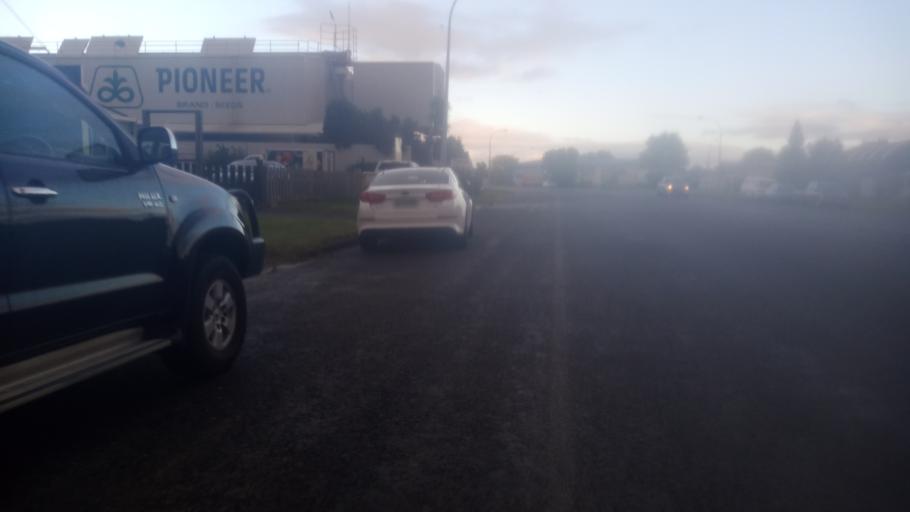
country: NZ
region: Gisborne
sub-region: Gisborne District
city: Gisborne
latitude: -38.6656
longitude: 177.9949
